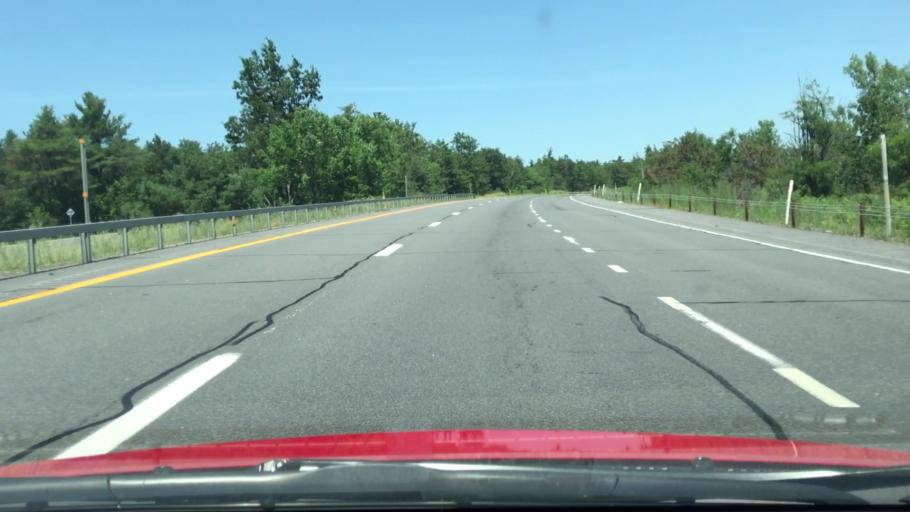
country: US
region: New York
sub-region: Essex County
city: Keeseville
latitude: 44.4957
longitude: -73.5000
